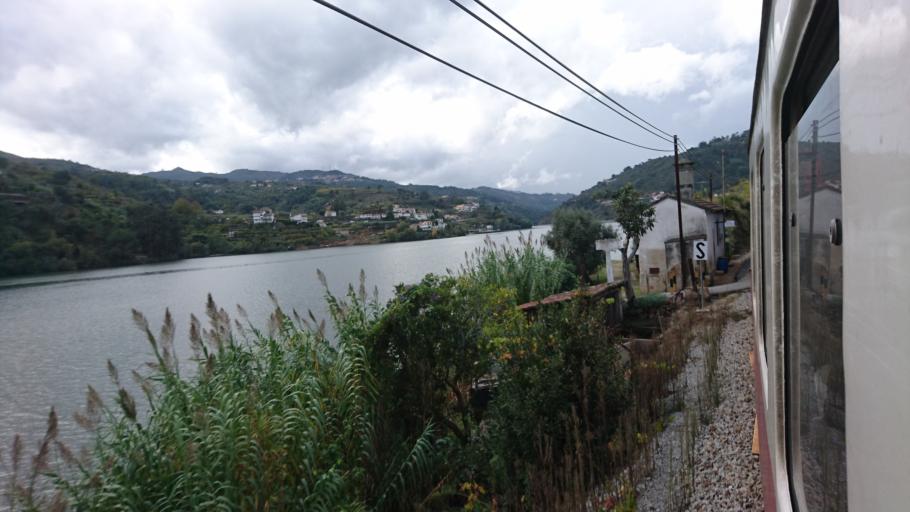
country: PT
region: Viseu
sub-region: Resende
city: Resende
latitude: 41.1065
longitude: -8.0038
